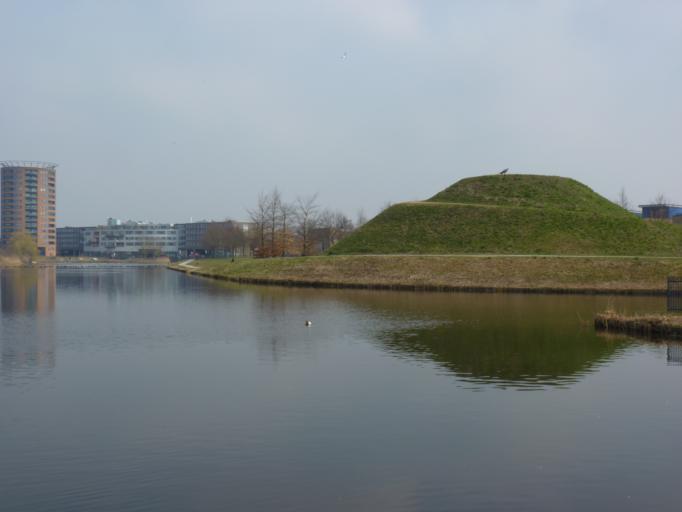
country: NL
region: Utrecht
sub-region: Gemeente Amersfoort
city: Hoogland
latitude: 52.1990
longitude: 5.3694
